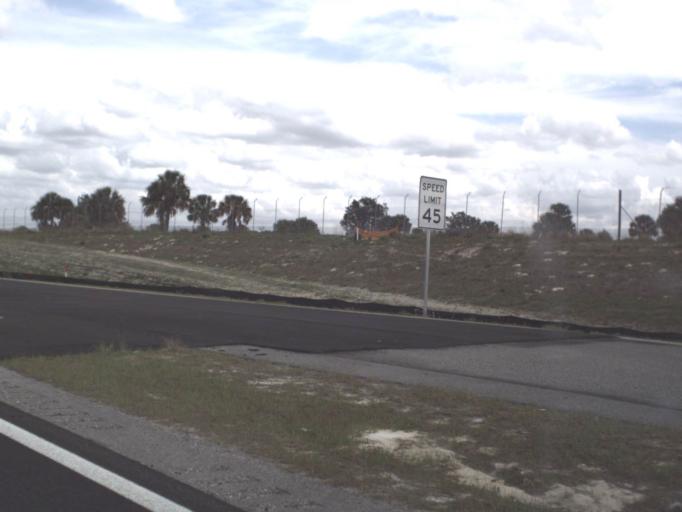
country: US
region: Florida
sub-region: Lake County
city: Mount Plymouth
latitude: 28.7838
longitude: -81.5212
